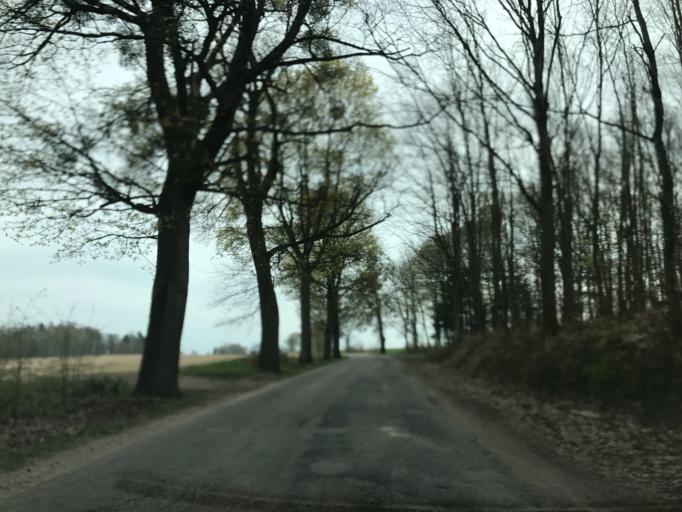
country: PL
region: Warmian-Masurian Voivodeship
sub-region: Powiat ostrodzki
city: Gierzwald
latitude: 53.6424
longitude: 20.0942
